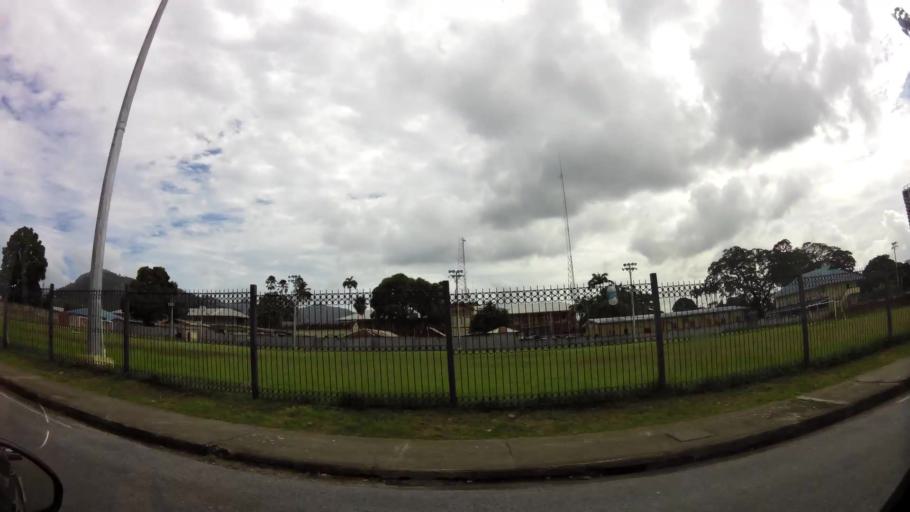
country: TT
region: City of Port of Spain
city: Port-of-Spain
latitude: 10.6719
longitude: -61.5295
